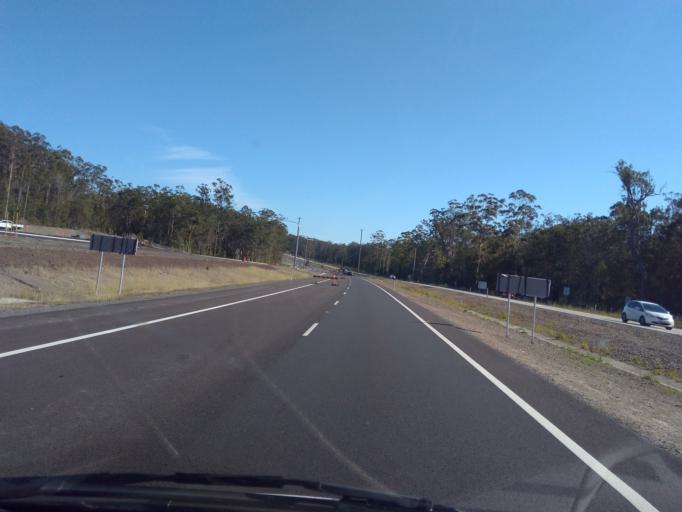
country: AU
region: New South Wales
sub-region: Kempsey
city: Crescent Head
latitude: -31.2480
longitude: 152.8218
